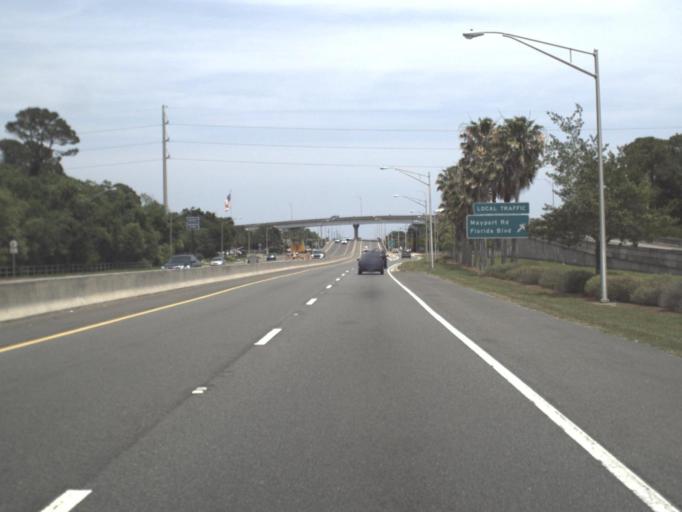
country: US
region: Florida
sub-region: Duval County
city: Atlantic Beach
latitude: 30.3243
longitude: -81.4246
